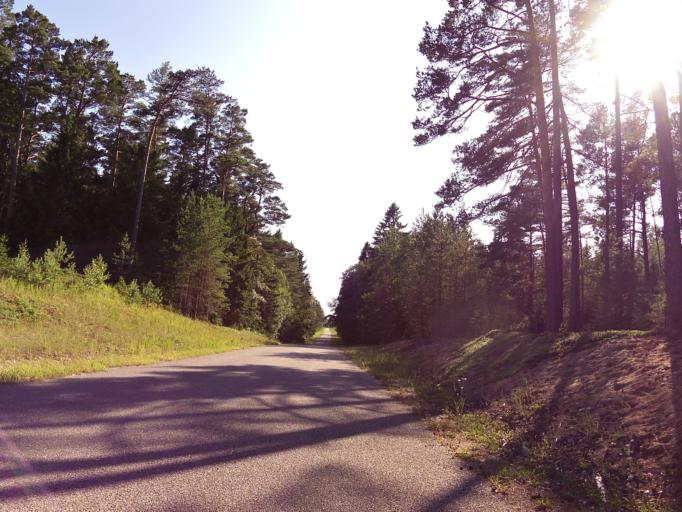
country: EE
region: Hiiumaa
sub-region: Kaerdla linn
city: Kardla
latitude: 58.9071
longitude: 22.2895
